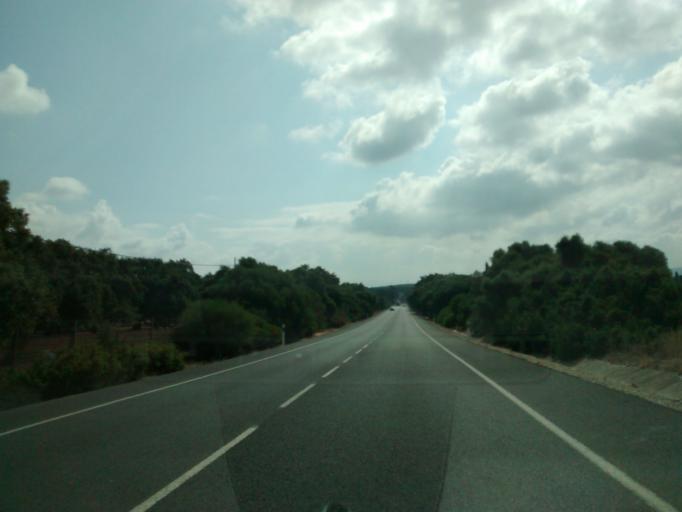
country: ES
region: Andalusia
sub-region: Provincia de Cadiz
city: Vejer de la Frontera
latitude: 36.2516
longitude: -5.9306
